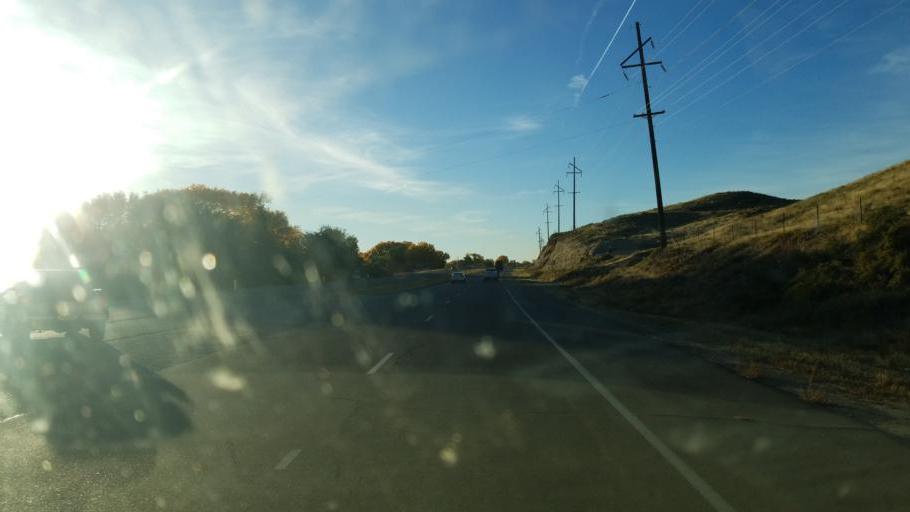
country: US
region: New Mexico
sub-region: San Juan County
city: Lee Acres
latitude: 36.7076
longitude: -108.1259
